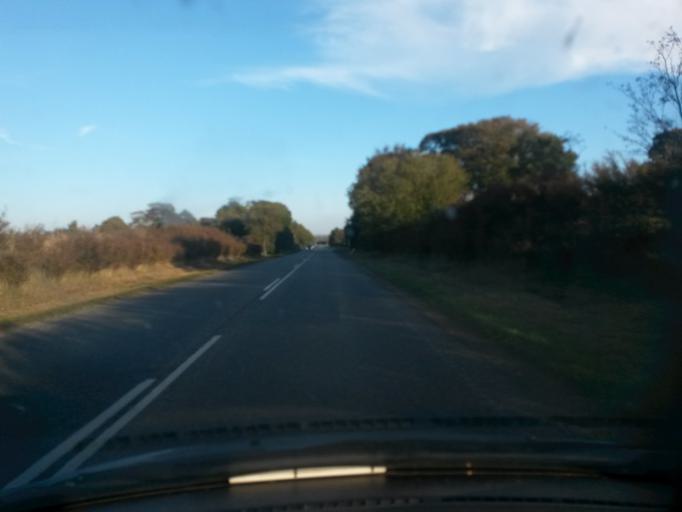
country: DK
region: Central Jutland
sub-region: Viborg Kommune
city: Karup
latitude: 56.3036
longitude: 9.3006
